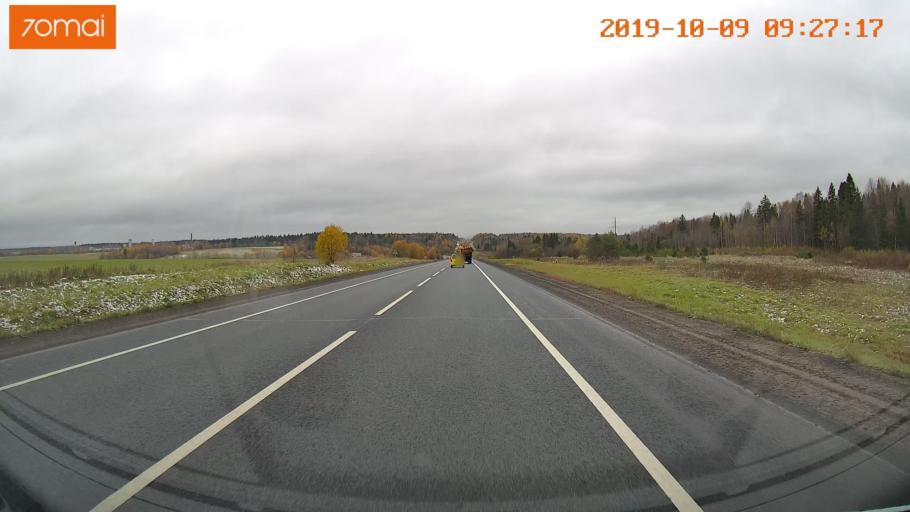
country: RU
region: Vologda
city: Vologda
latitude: 59.1111
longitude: 39.9804
